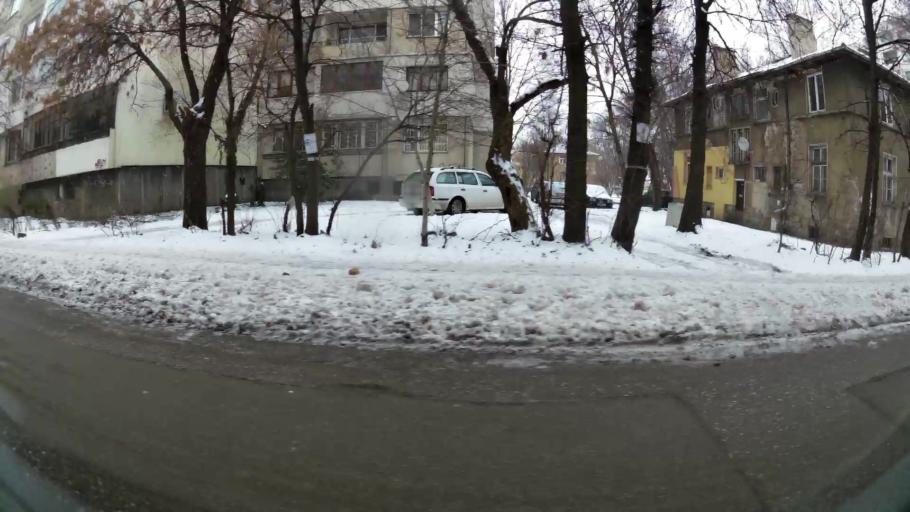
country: BG
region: Sofia-Capital
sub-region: Stolichna Obshtina
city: Sofia
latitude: 42.7130
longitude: 23.3019
